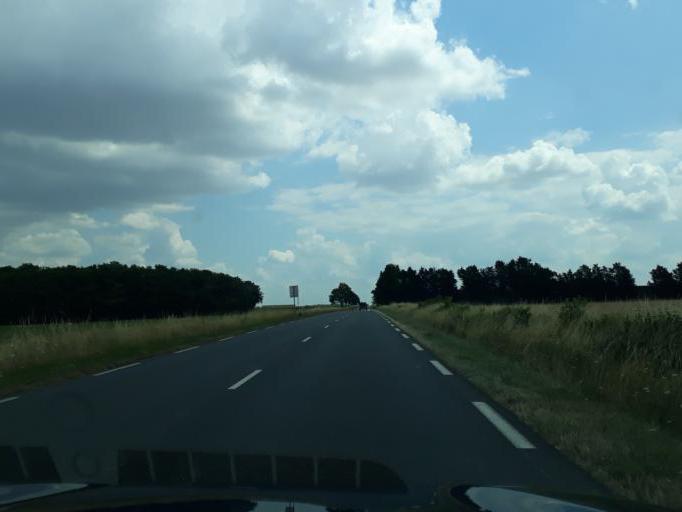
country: FR
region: Centre
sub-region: Departement du Cher
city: Avord
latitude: 47.0341
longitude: 2.6272
